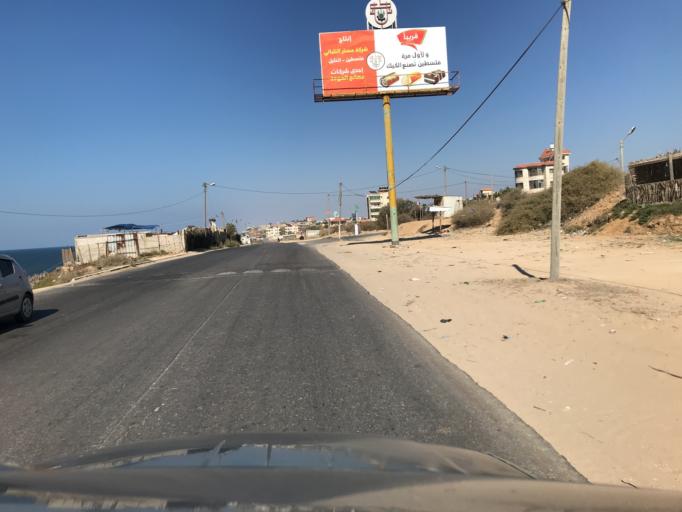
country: PS
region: Gaza Strip
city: Az Zuwaydah
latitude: 31.4480
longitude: 34.3608
